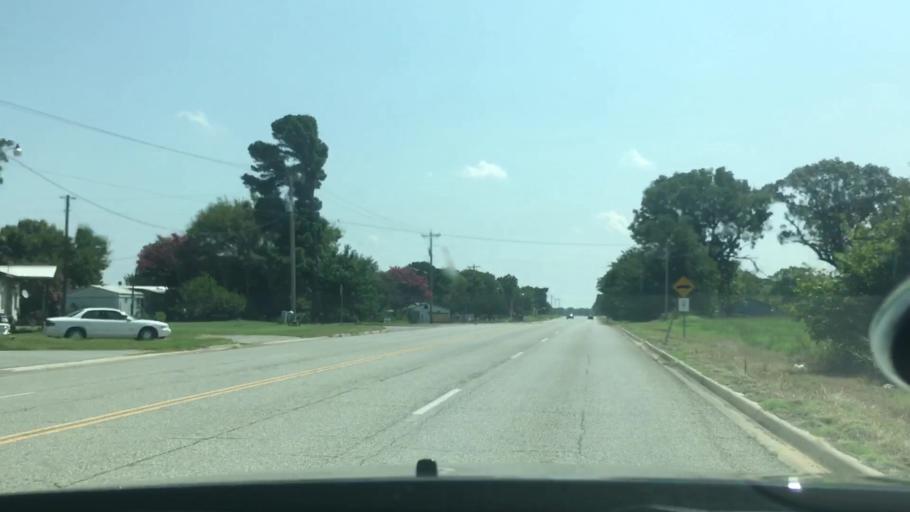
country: US
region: Oklahoma
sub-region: Atoka County
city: Atoka
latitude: 34.3005
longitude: -95.9924
